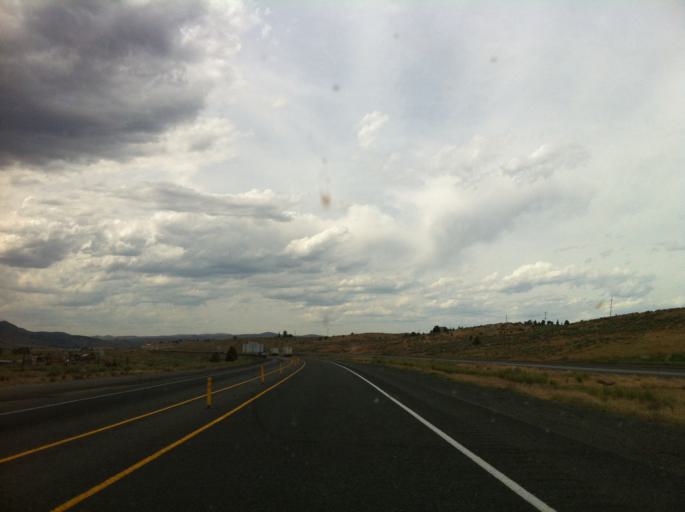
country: US
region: Oregon
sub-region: Baker County
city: Baker City
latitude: 44.5535
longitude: -117.4243
